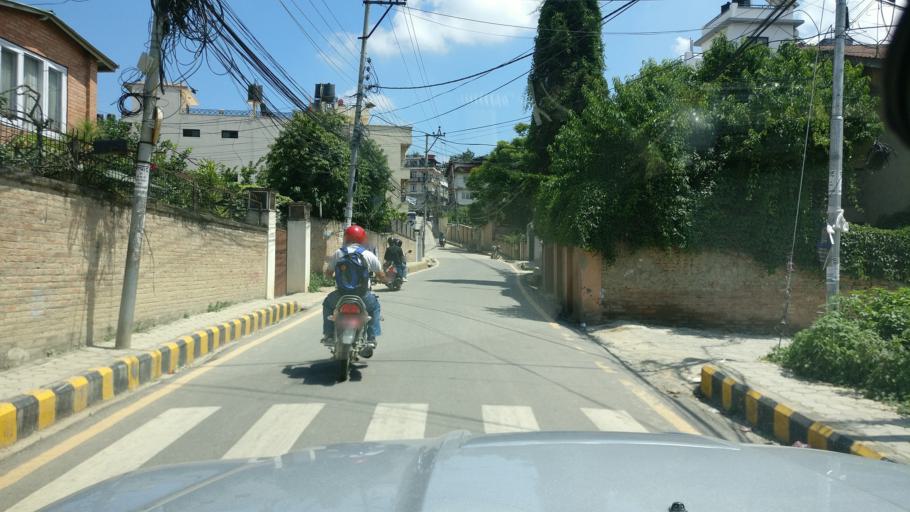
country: NP
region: Central Region
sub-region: Bagmati Zone
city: Patan
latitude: 27.6834
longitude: 85.3049
